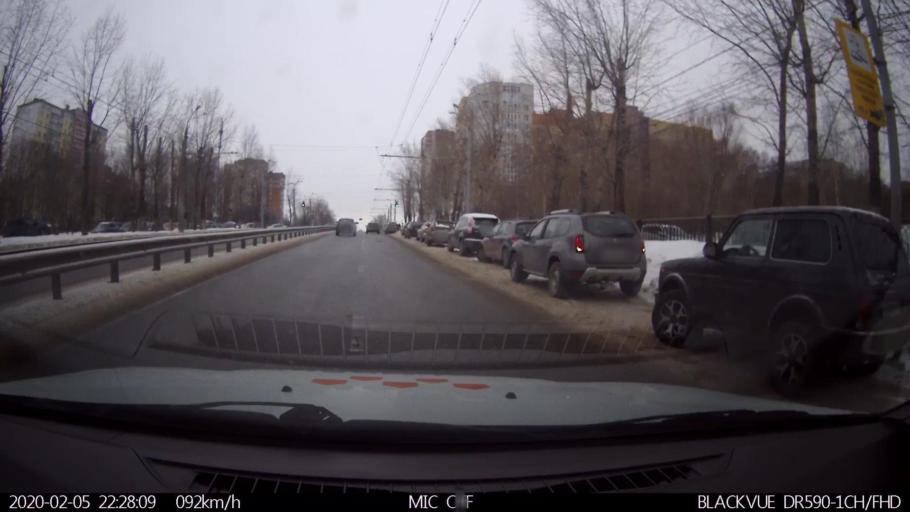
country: RU
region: Nizjnij Novgorod
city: Imeni Stepana Razina
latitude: 54.7598
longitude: 44.1272
